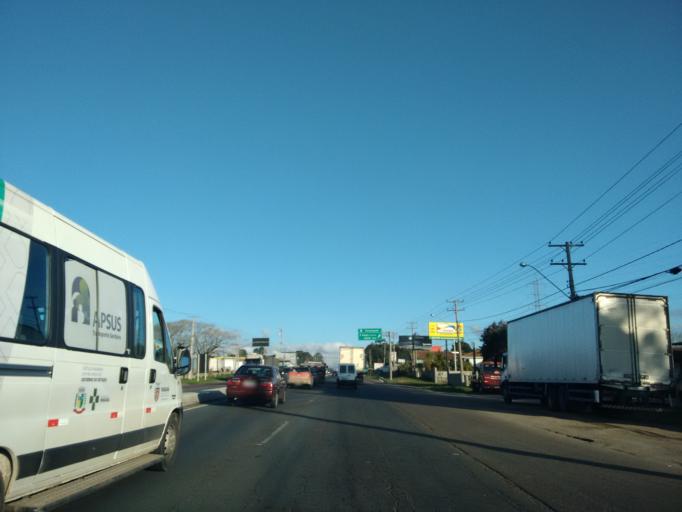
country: BR
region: Parana
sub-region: Sao Jose Dos Pinhais
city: Sao Jose dos Pinhais
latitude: -25.5603
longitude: -49.1848
